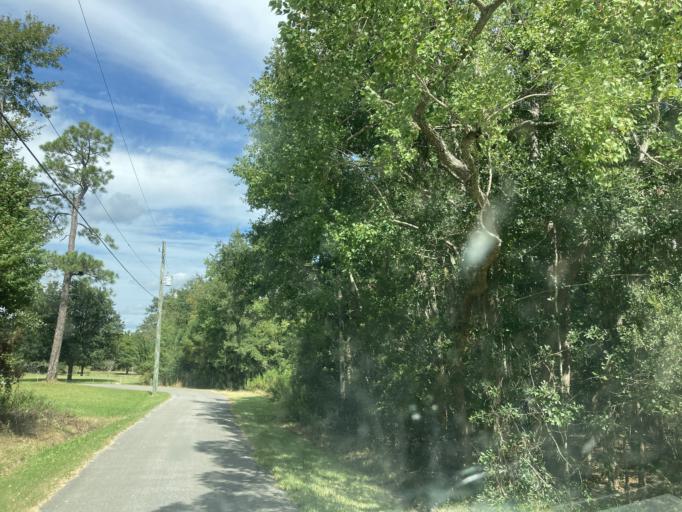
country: US
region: Mississippi
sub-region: Jackson County
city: Saint Martin
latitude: 30.4288
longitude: -88.8771
